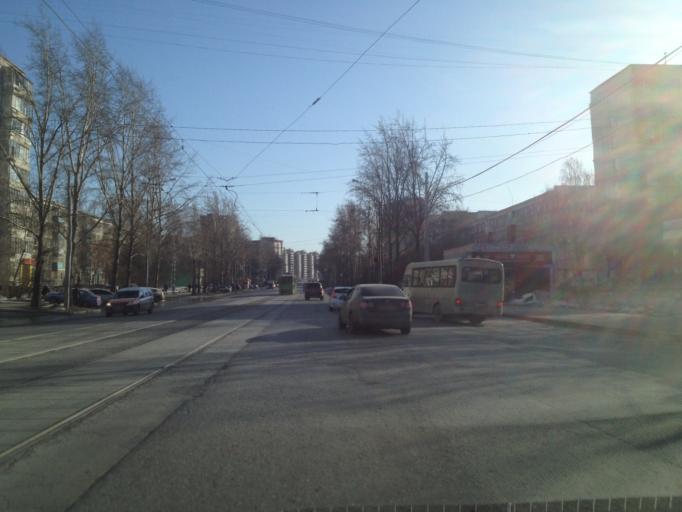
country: RU
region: Sverdlovsk
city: Sovkhoznyy
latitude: 56.8305
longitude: 60.5447
